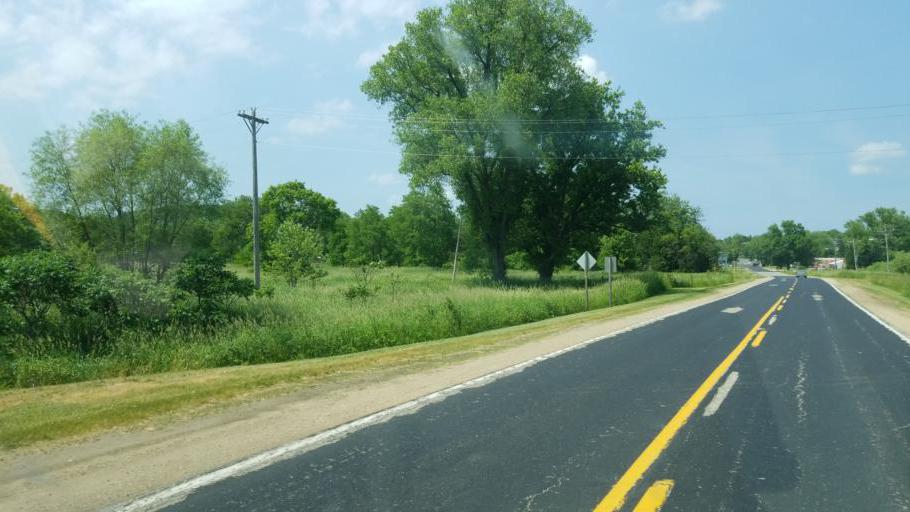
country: US
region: Wisconsin
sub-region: Monroe County
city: Cashton
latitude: 43.5688
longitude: -90.6364
